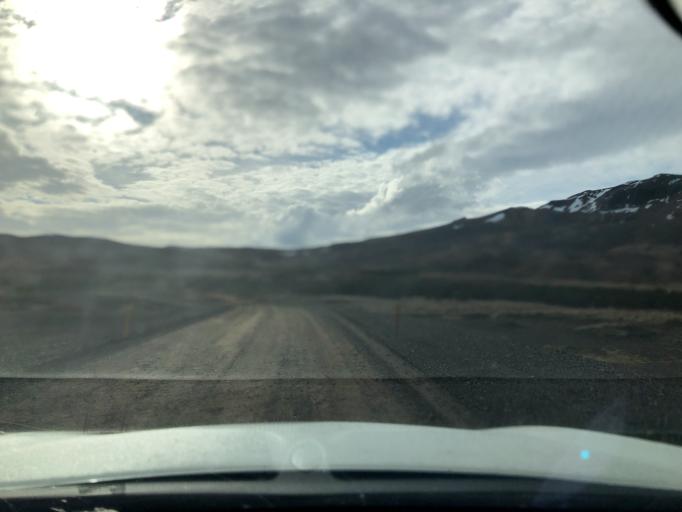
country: IS
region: West
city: Stykkisholmur
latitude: 64.9956
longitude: -22.7455
